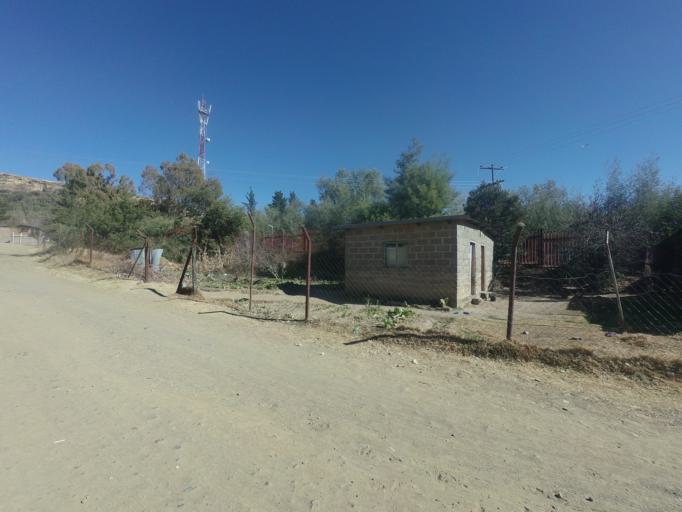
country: LS
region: Maseru
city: Nako
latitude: -29.4532
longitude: 27.7244
